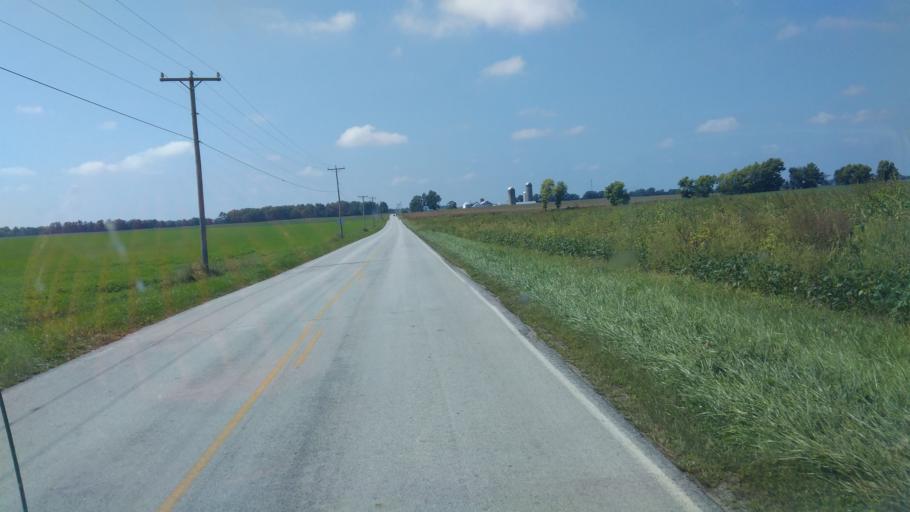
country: US
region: Ohio
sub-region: Hardin County
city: Kenton
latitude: 40.6663
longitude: -83.5775
